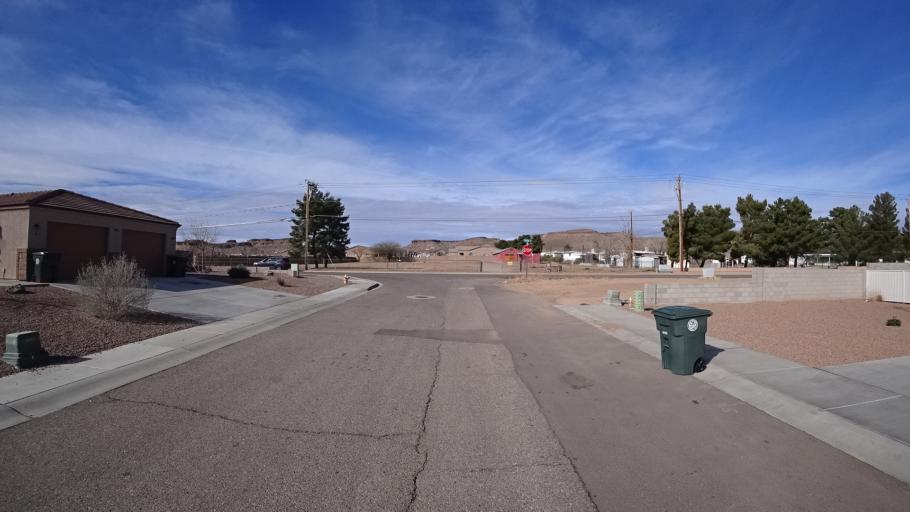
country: US
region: Arizona
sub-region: Mohave County
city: Kingman
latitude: 35.2200
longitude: -114.0442
